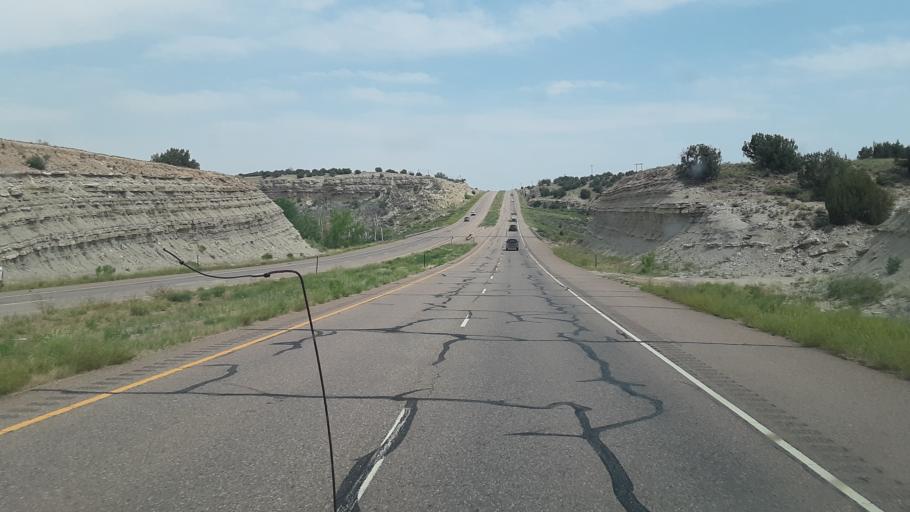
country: US
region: Colorado
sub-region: Fremont County
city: Penrose
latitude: 38.3789
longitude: -104.9513
